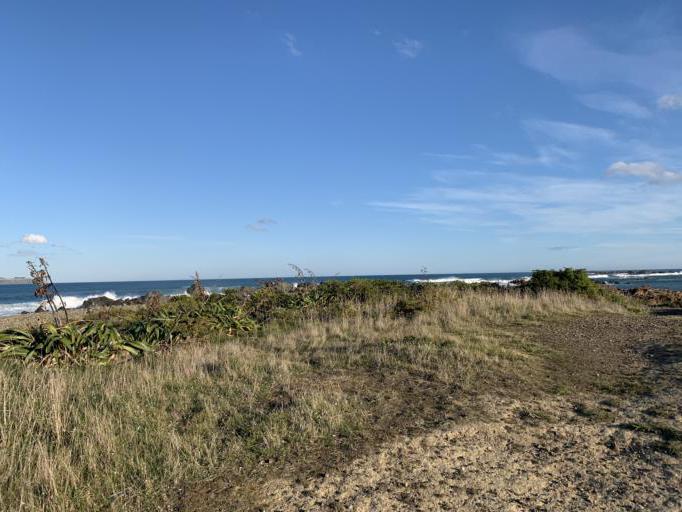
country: NZ
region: Wellington
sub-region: Wellington City
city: Wellington
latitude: -41.3436
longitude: 174.8210
